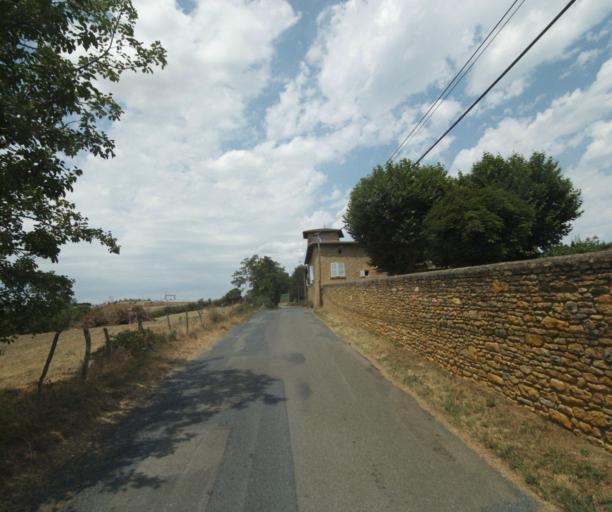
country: FR
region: Rhone-Alpes
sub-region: Departement du Rhone
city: Saint-Germain-Nuelles
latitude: 45.8602
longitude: 4.5996
